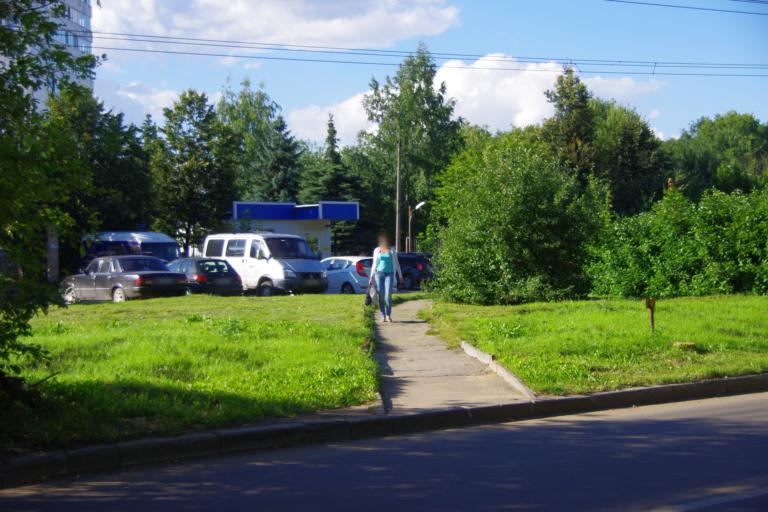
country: RU
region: Moskovskaya
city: Krasnogorsk
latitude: 55.8351
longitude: 37.3104
